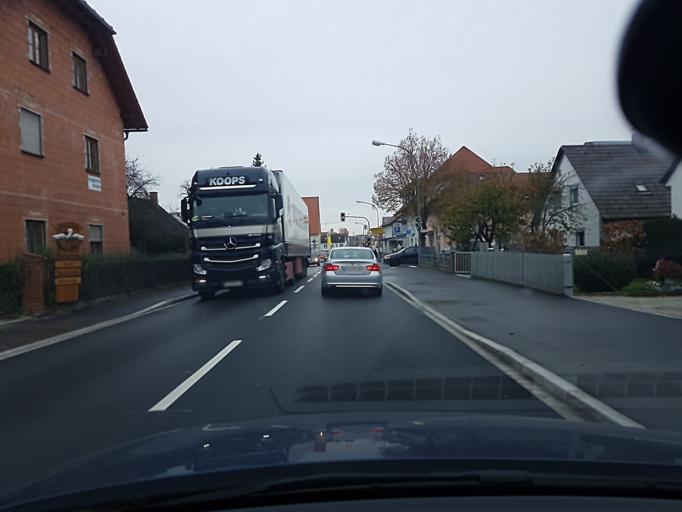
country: DE
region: Bavaria
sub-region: Lower Bavaria
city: Essenbach
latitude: 48.6107
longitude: 12.2136
